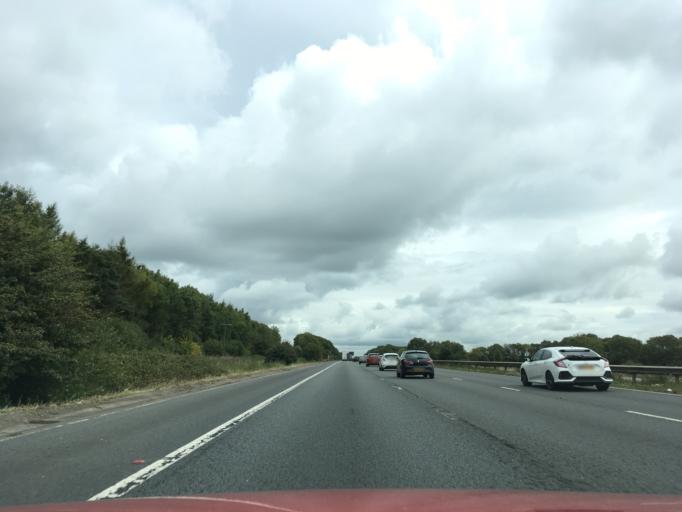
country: GB
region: England
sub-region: South Gloucestershire
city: Tytherington
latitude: 51.5913
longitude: -2.4925
